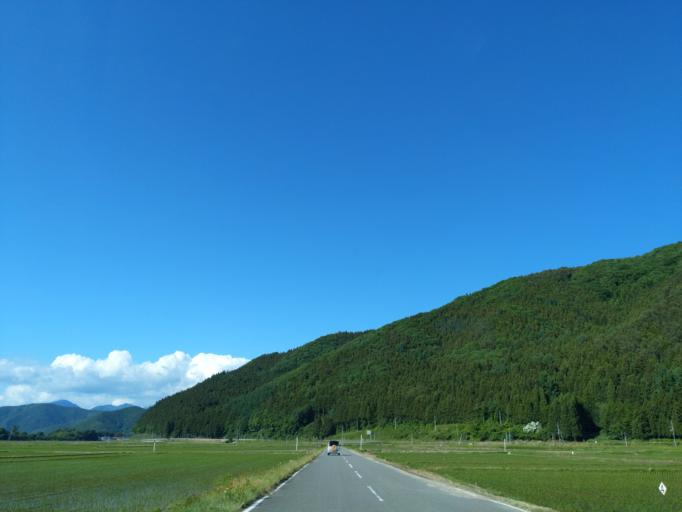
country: JP
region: Fukushima
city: Inawashiro
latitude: 37.4277
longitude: 140.1445
